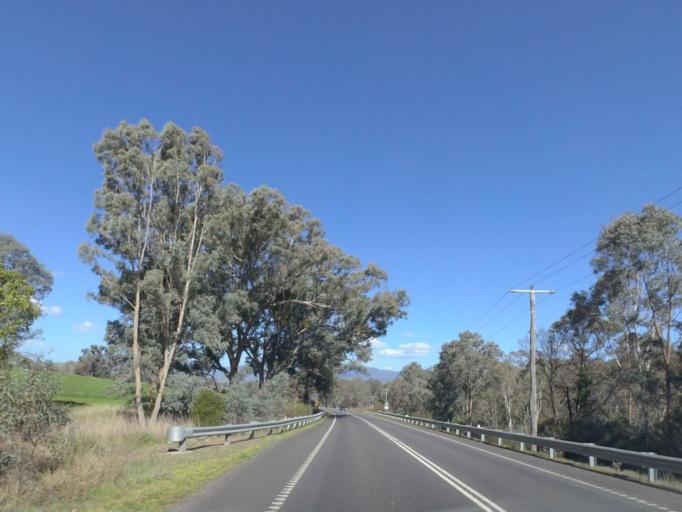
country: AU
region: Victoria
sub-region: Murrindindi
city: Alexandra
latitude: -37.2120
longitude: 145.7324
